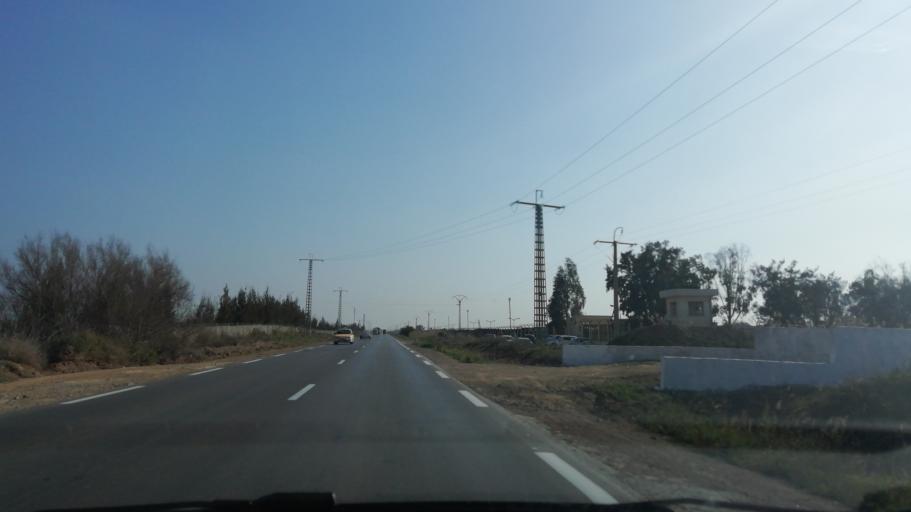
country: DZ
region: Mostaganem
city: Mostaganem
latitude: 35.7466
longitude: 0.0217
